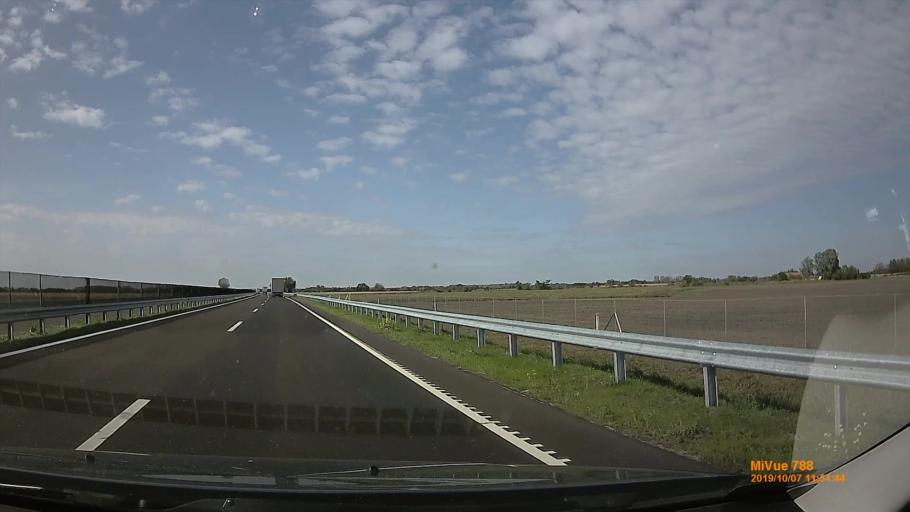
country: HU
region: Bekes
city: Szarvas
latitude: 46.8198
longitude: 20.5857
